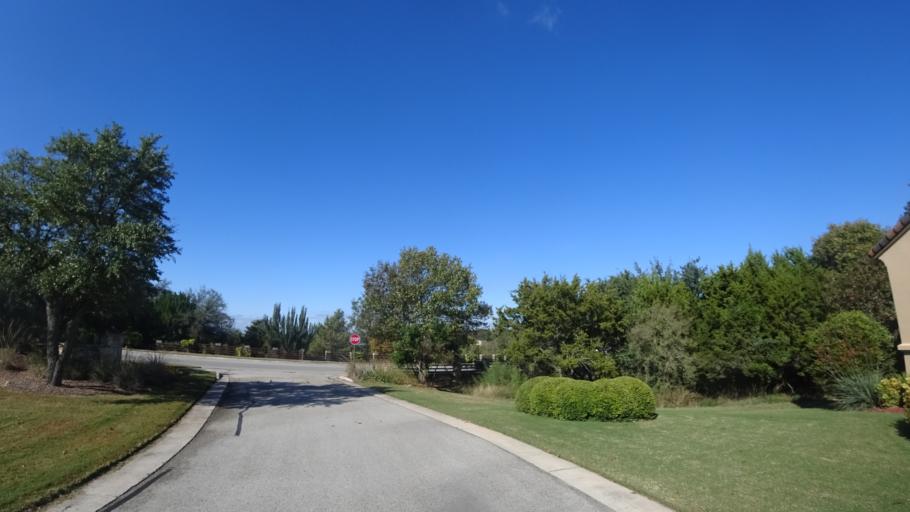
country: US
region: Texas
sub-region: Travis County
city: Hudson Bend
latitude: 30.3648
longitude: -97.8863
